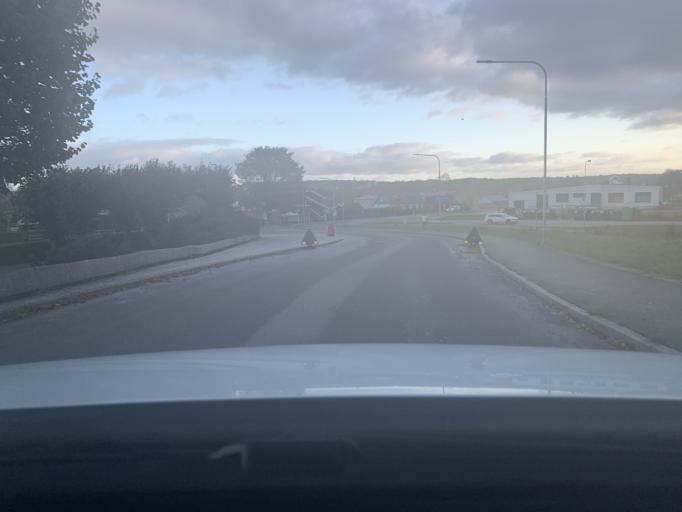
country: SE
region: Skane
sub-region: Horby Kommun
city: Hoerby
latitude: 55.8449
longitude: 13.6556
